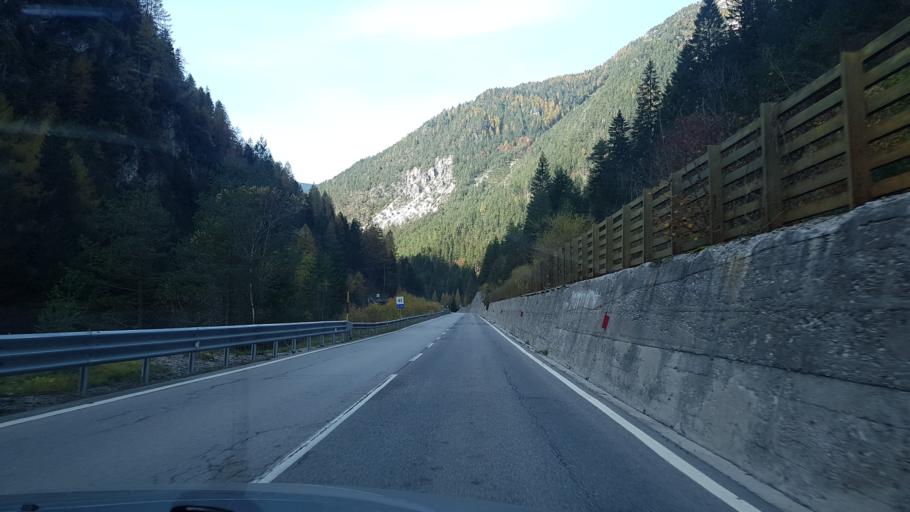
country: IT
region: Veneto
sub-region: Provincia di Belluno
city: San Pietro di Cadore
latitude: 46.5798
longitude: 12.6331
